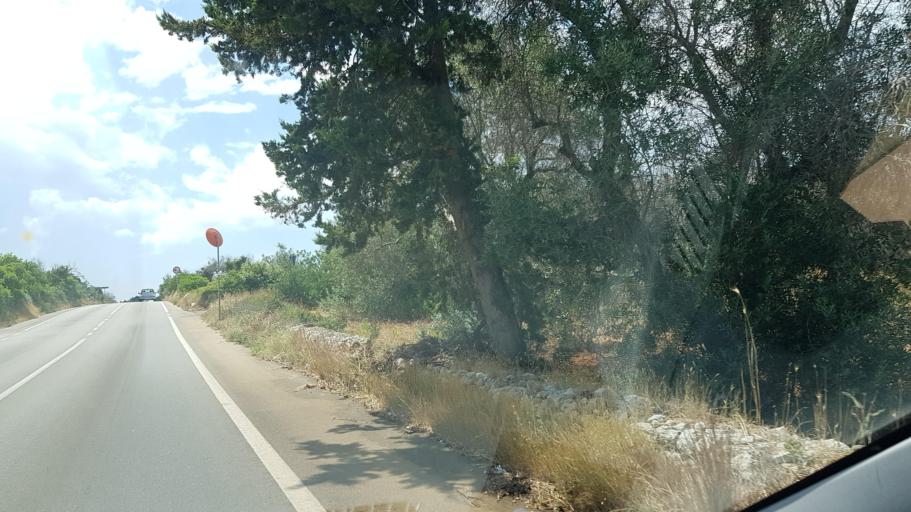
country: IT
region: Apulia
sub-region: Provincia di Lecce
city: Ruffano
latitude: 39.9604
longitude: 18.2449
